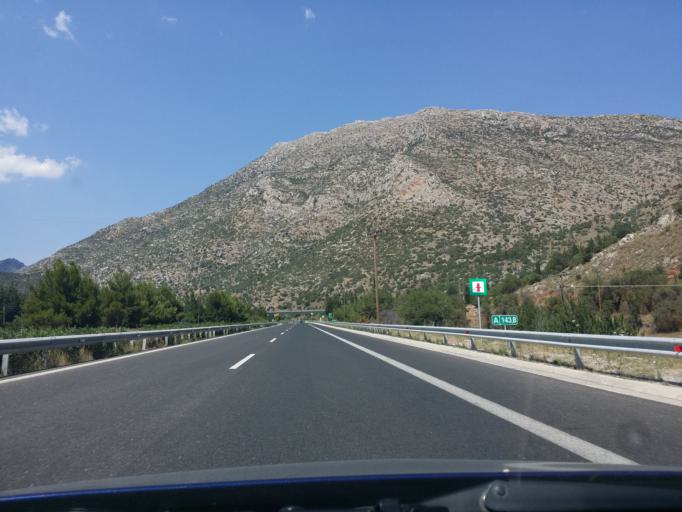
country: GR
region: Peloponnese
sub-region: Nomos Arkadias
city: Tripoli
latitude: 37.6223
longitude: 22.4627
